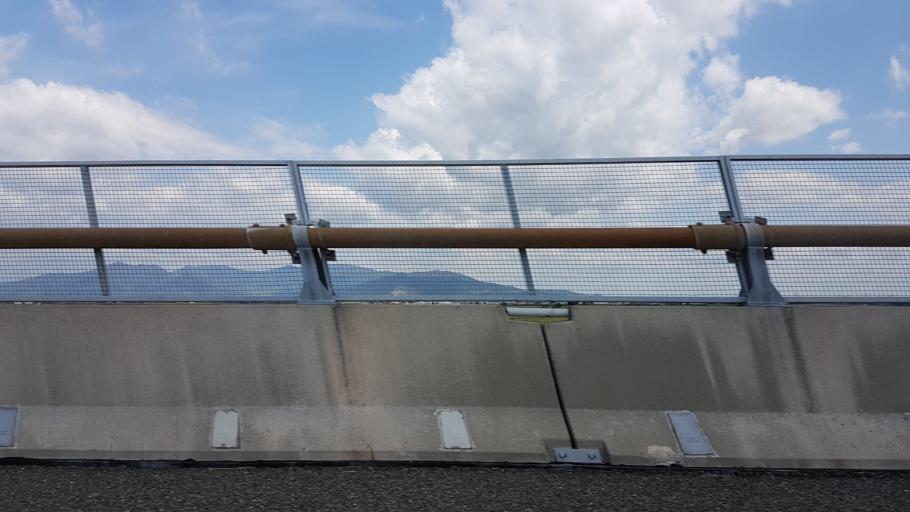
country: IT
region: Tuscany
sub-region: Provincia di Livorno
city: Vicarello
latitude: 43.6159
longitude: 10.4366
